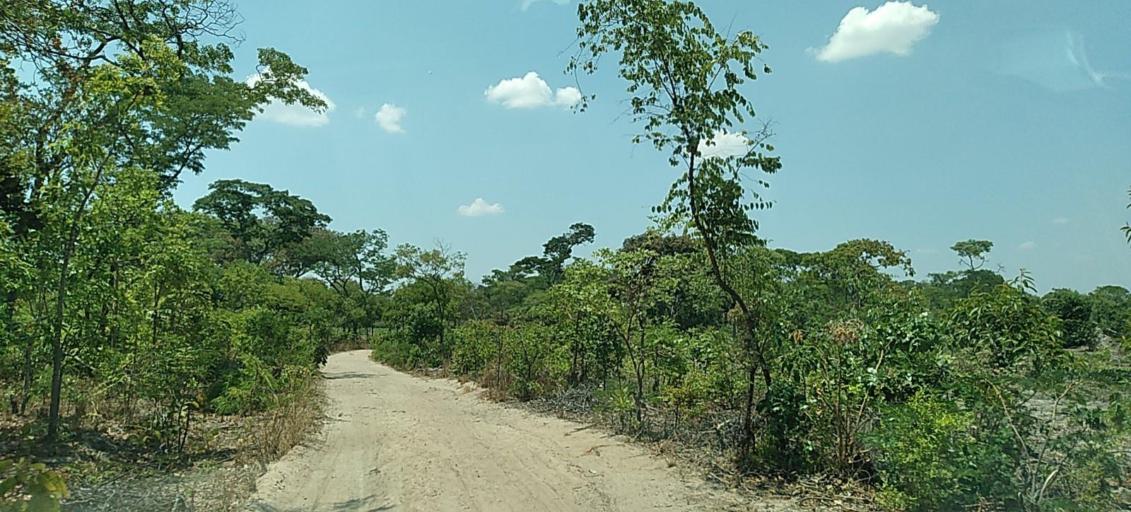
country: ZM
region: Copperbelt
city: Mpongwe
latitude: -13.6502
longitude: 28.4869
